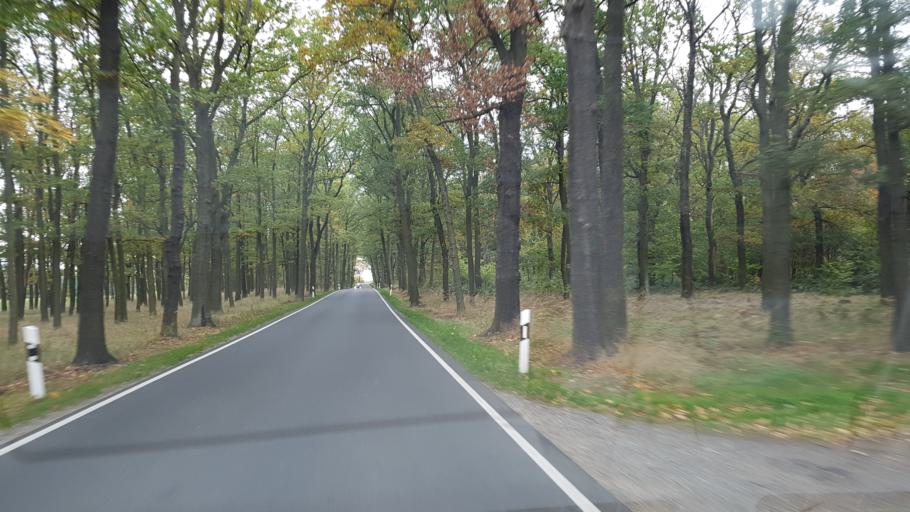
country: DE
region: Saxony
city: Falkenhain
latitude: 51.3804
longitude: 12.9069
